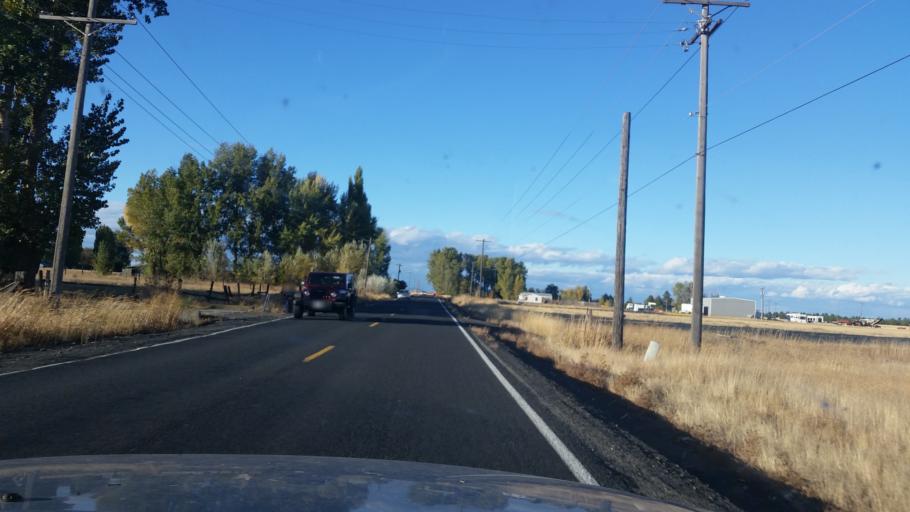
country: US
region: Washington
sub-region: Spokane County
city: Airway Heights
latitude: 47.6088
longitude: -117.6075
